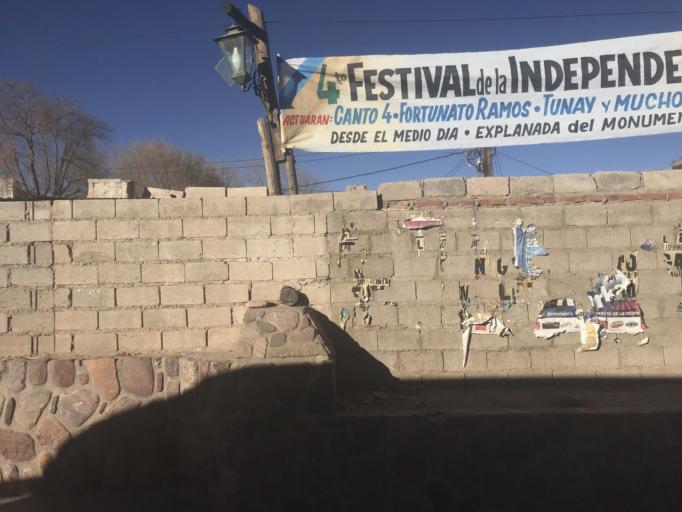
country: AR
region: Jujuy
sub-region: Departamento de Humahuaca
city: Humahuaca
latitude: -23.2039
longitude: -65.3471
